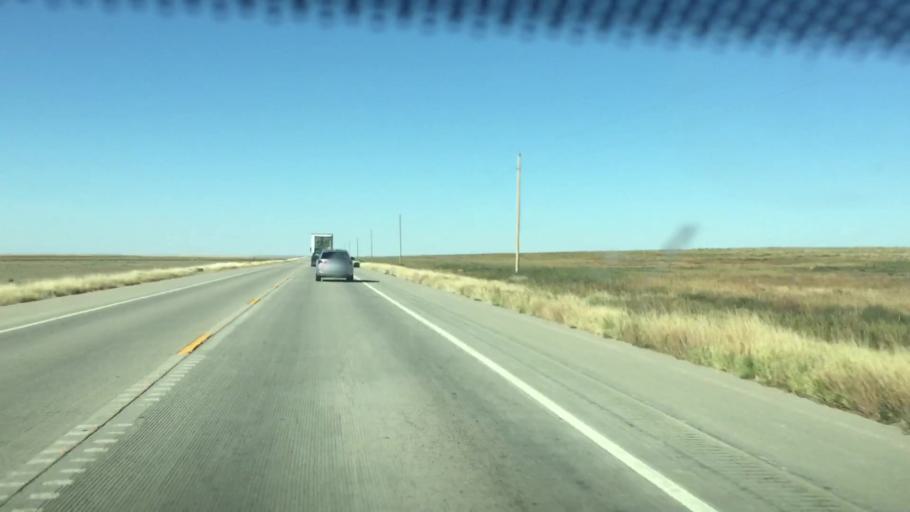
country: US
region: Colorado
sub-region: Kiowa County
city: Eads
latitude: 38.3063
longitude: -102.7199
